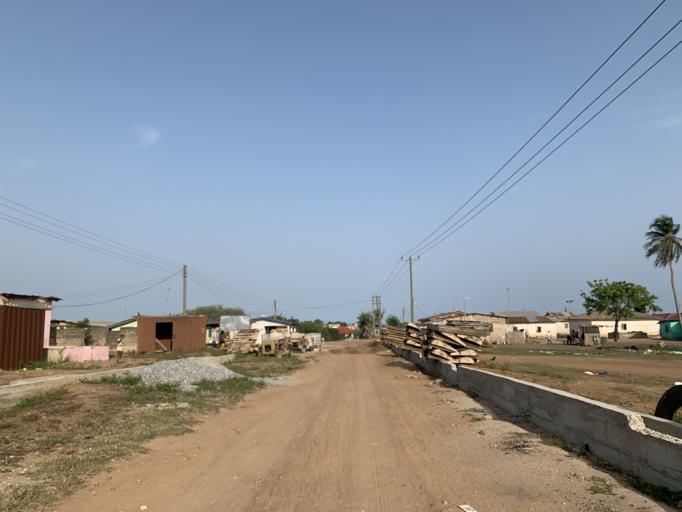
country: GH
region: Central
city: Winneba
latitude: 5.3785
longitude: -0.6149
